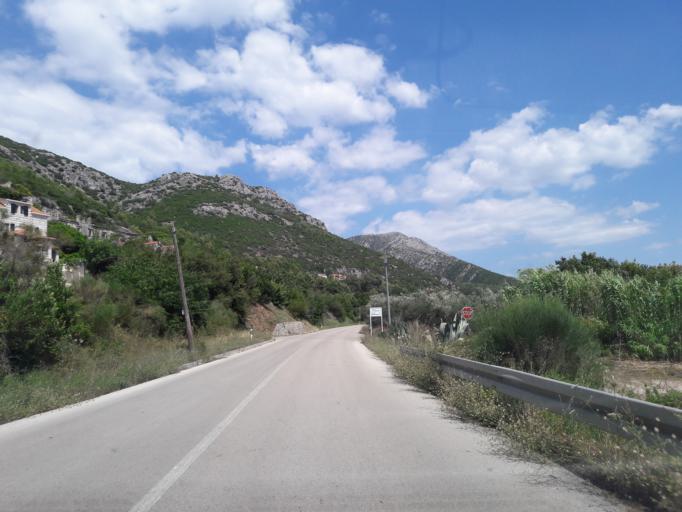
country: HR
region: Dubrovacko-Neretvanska
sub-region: Grad Korcula
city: Zrnovo
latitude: 42.9864
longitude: 17.0915
